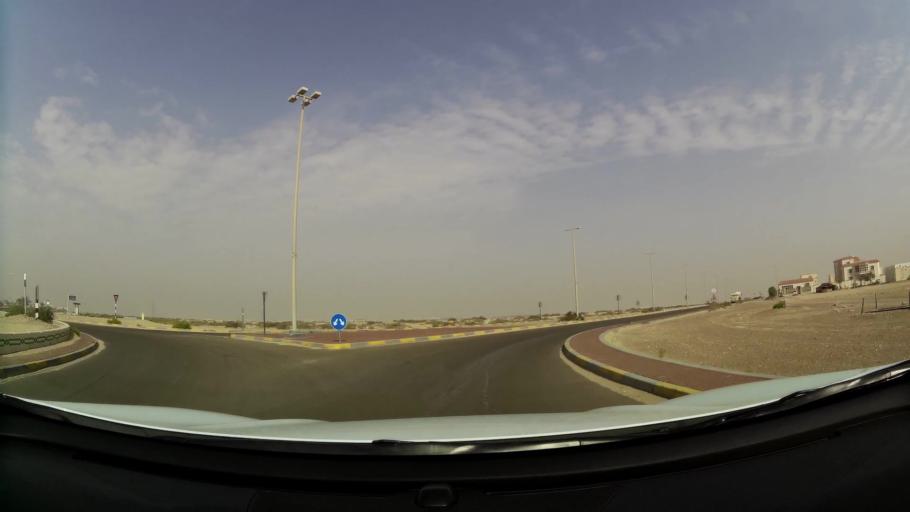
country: AE
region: Abu Dhabi
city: Abu Dhabi
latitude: 24.2761
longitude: 54.6843
